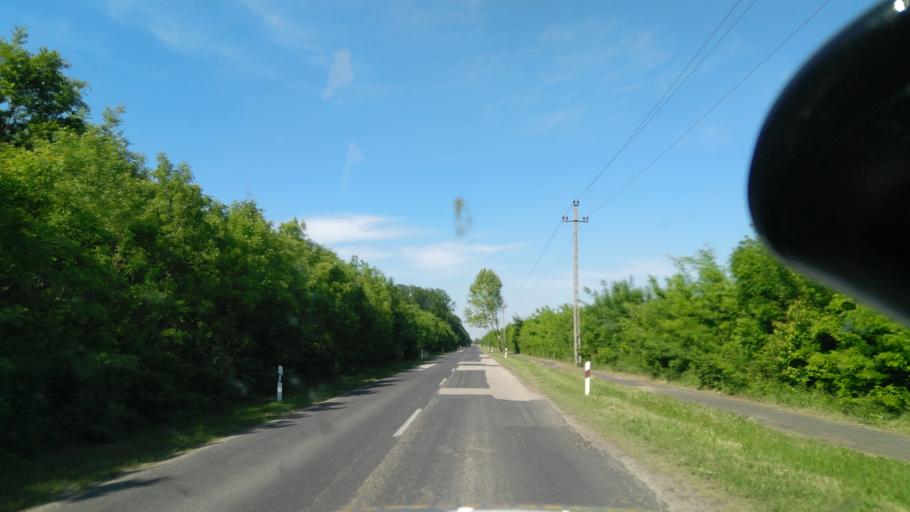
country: HU
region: Bekes
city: Gyula
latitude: 46.7070
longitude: 21.3187
